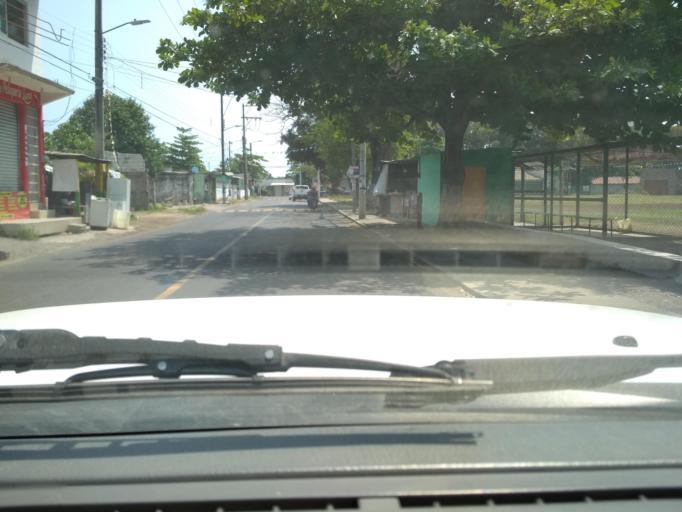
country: MX
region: Veracruz
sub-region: Medellin
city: Fraccionamiento Arboledas San Ramon
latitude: 19.0941
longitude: -96.1427
